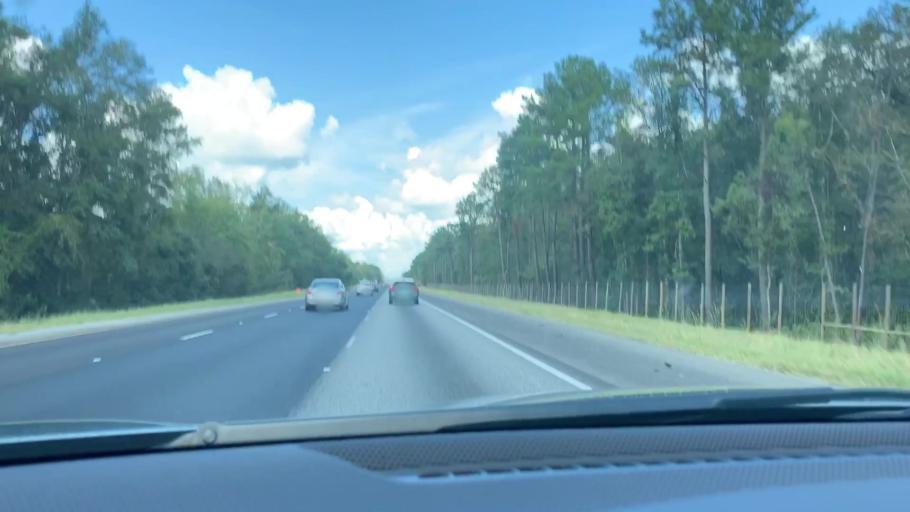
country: US
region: Georgia
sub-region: Camden County
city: Woodbine
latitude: 30.9080
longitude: -81.6858
